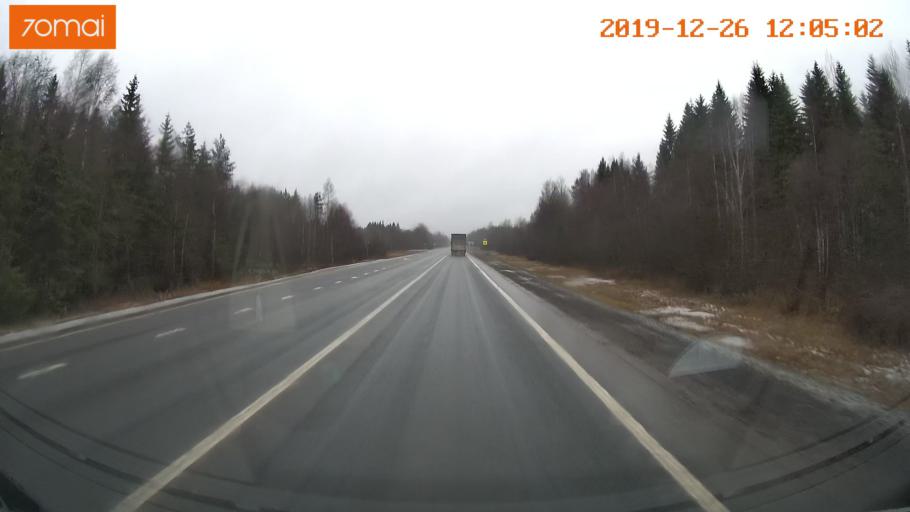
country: RU
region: Vologda
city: Tonshalovo
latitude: 59.2979
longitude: 38.0880
